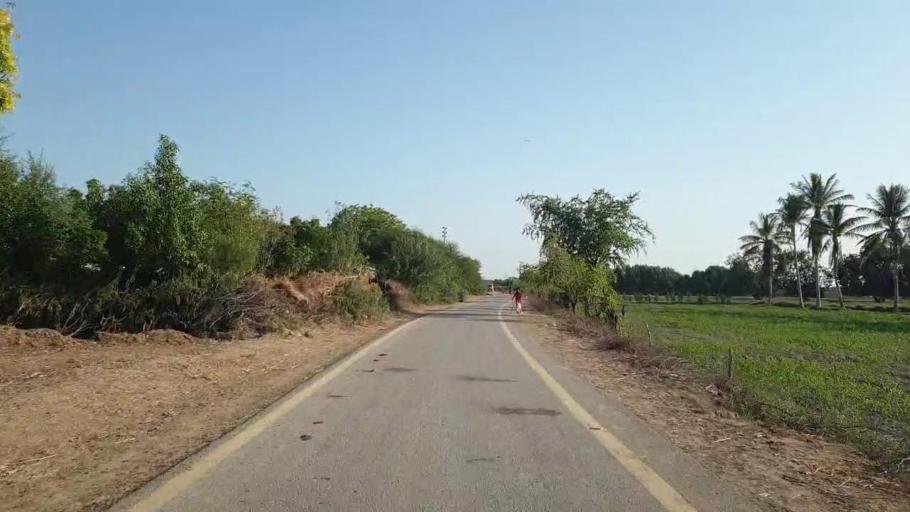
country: PK
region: Sindh
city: Hyderabad
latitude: 25.3332
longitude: 68.4228
